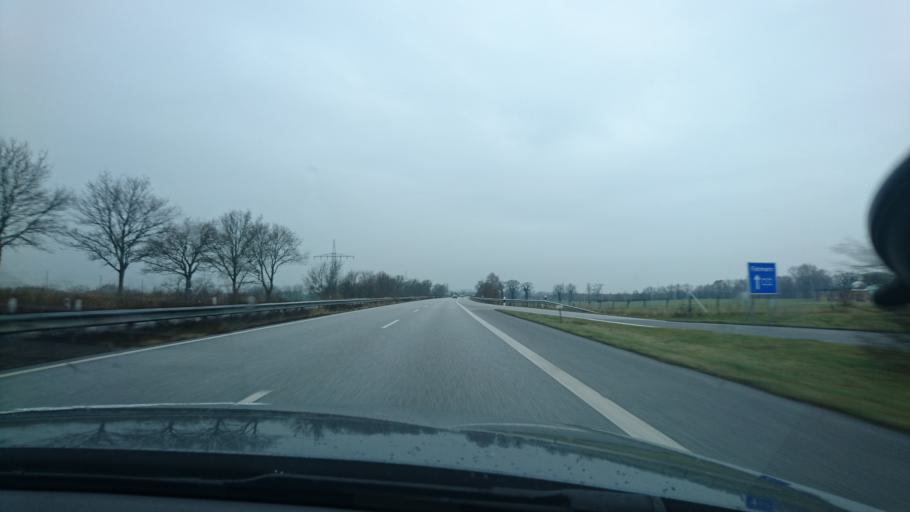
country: DE
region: Schleswig-Holstein
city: Lensahn
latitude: 54.2408
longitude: 10.8912
